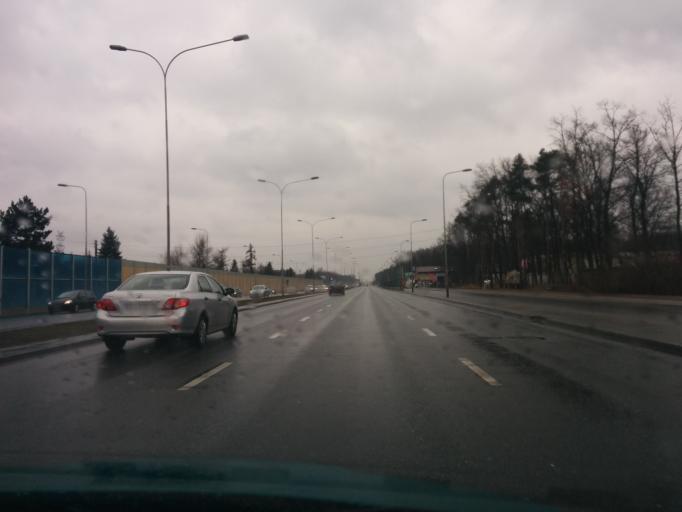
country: PL
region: Masovian Voivodeship
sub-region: Powiat legionowski
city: Jablonna
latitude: 52.3520
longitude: 20.9446
